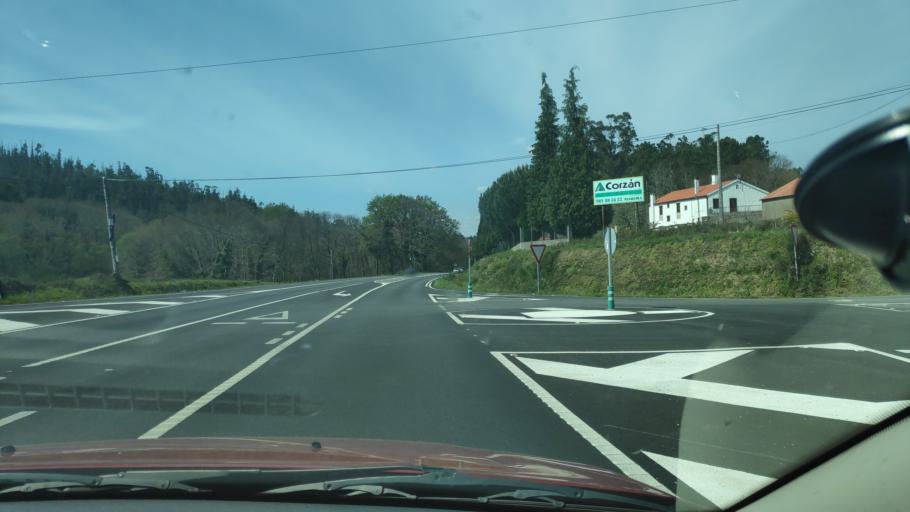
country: ES
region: Galicia
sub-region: Provincia da Coruna
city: Ames
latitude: 42.8854
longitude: -8.6835
